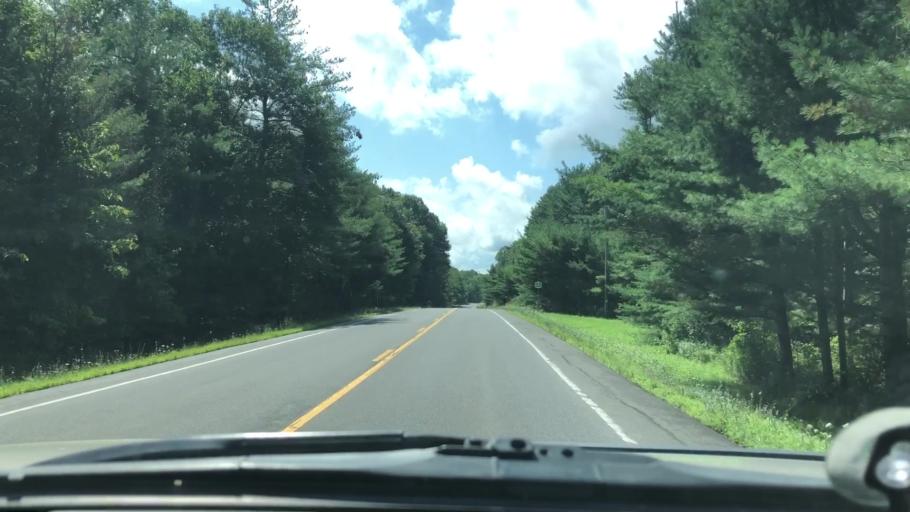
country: US
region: New York
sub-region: Greene County
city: Cairo
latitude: 42.2730
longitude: -73.9772
